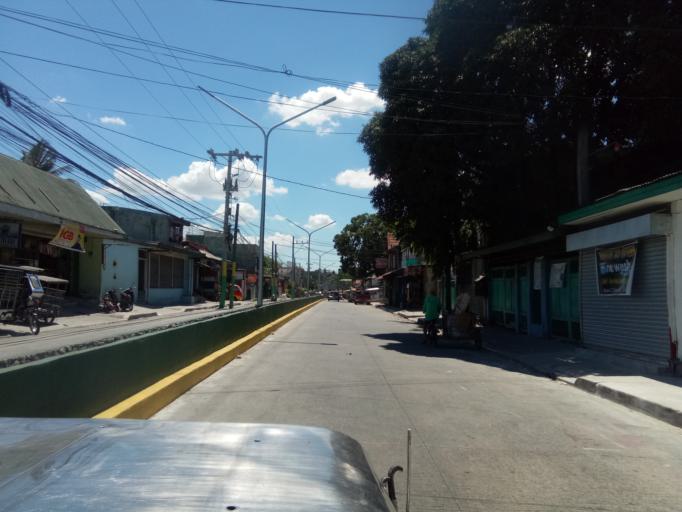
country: PH
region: Calabarzon
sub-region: Province of Cavite
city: Dasmarinas
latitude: 14.3182
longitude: 120.9691
